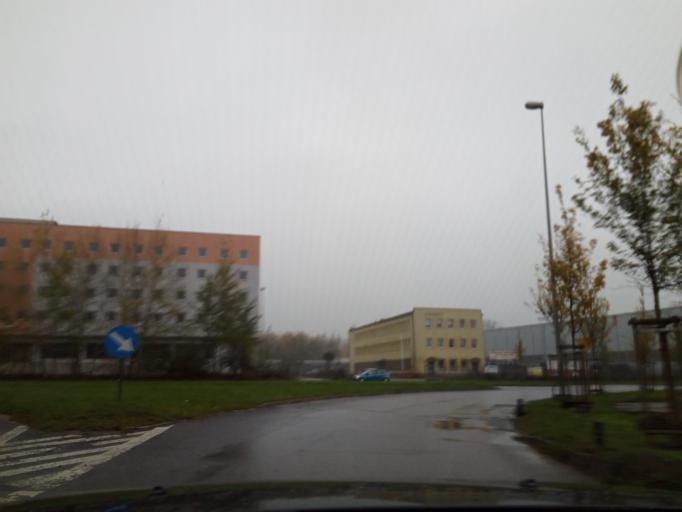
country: PL
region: Lesser Poland Voivodeship
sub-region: Powiat wielicki
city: Kokotow
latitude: 50.0876
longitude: 20.0654
